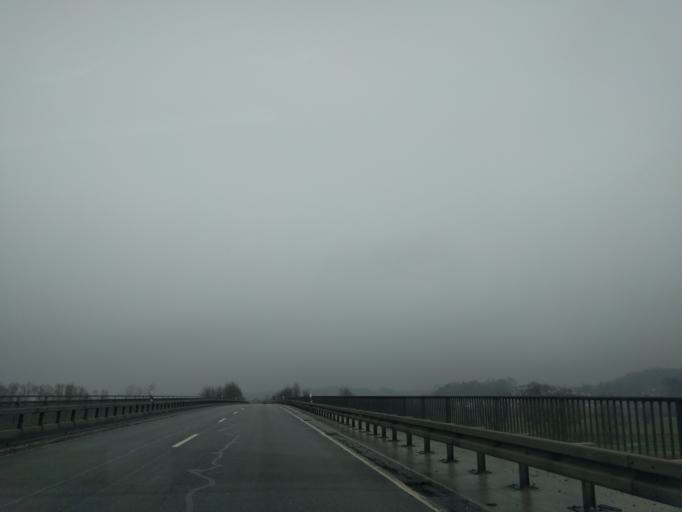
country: DE
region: Bavaria
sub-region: Lower Bavaria
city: Winzer
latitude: 48.7236
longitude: 13.0571
